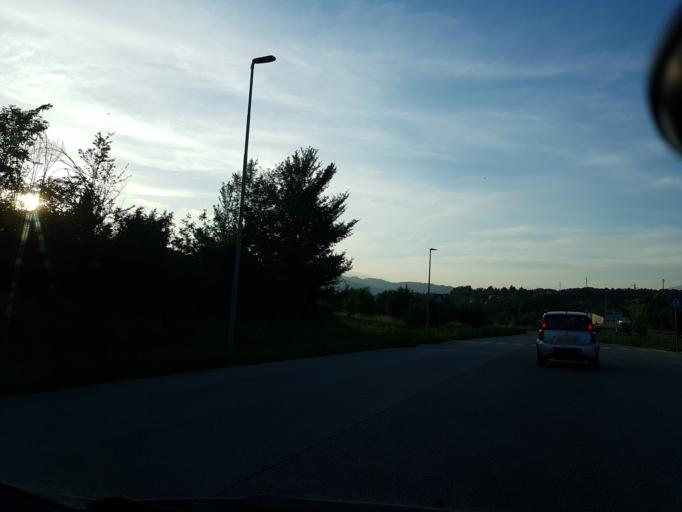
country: IT
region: Tuscany
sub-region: Provincia di Massa-Carrara
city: Aulla
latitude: 44.2190
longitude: 9.9763
